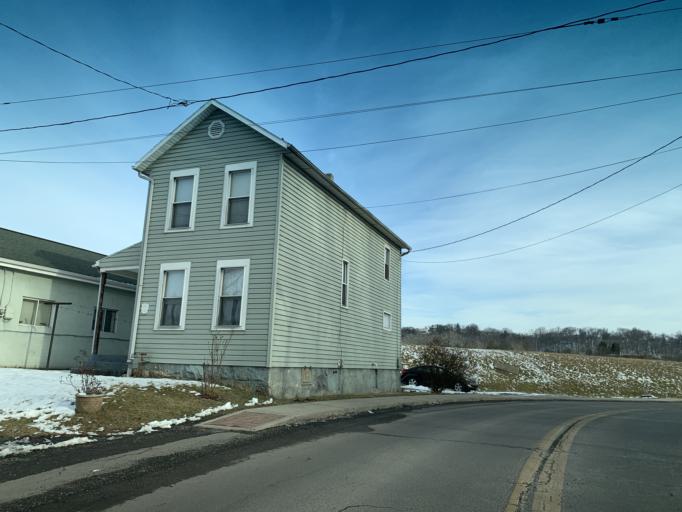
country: US
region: Maryland
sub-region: Allegany County
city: Cumberland
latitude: 39.6465
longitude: -78.7662
